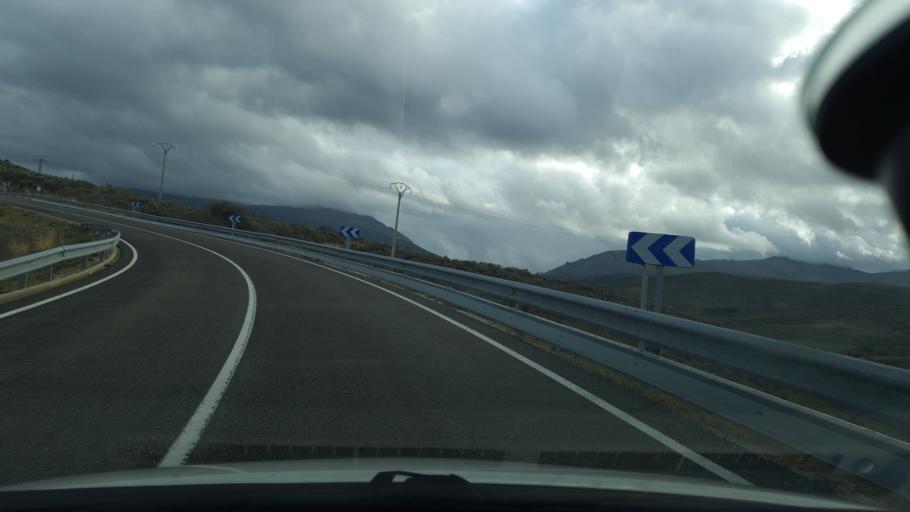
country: ES
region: Castille and Leon
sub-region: Provincia de Avila
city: San Martin del Pimpollar
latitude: 40.3886
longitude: -5.0168
